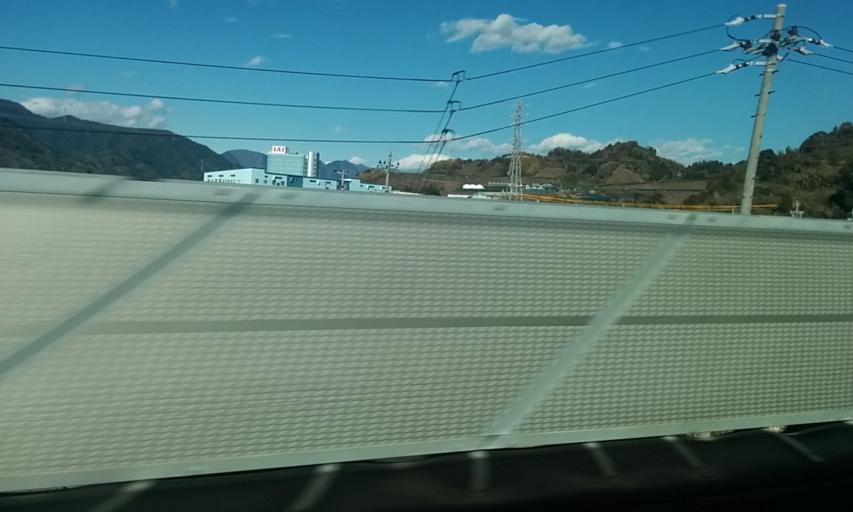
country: JP
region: Shizuoka
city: Shizuoka-shi
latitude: 35.0433
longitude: 138.4969
